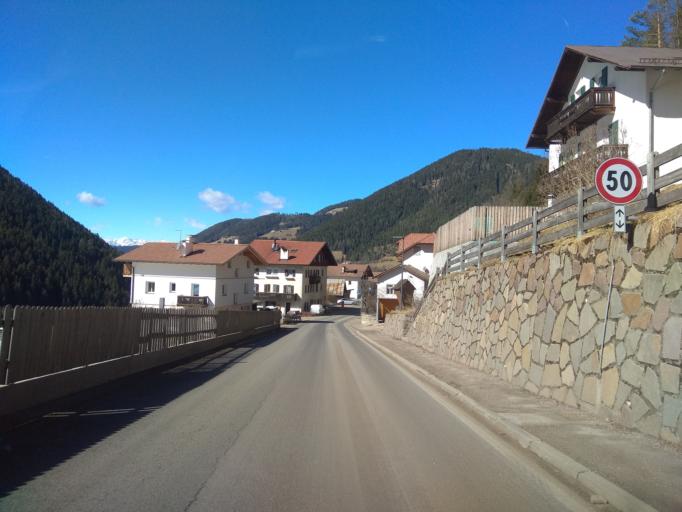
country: IT
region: Trentino-Alto Adige
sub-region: Bolzano
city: Nova Levante
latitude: 46.4252
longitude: 11.5514
